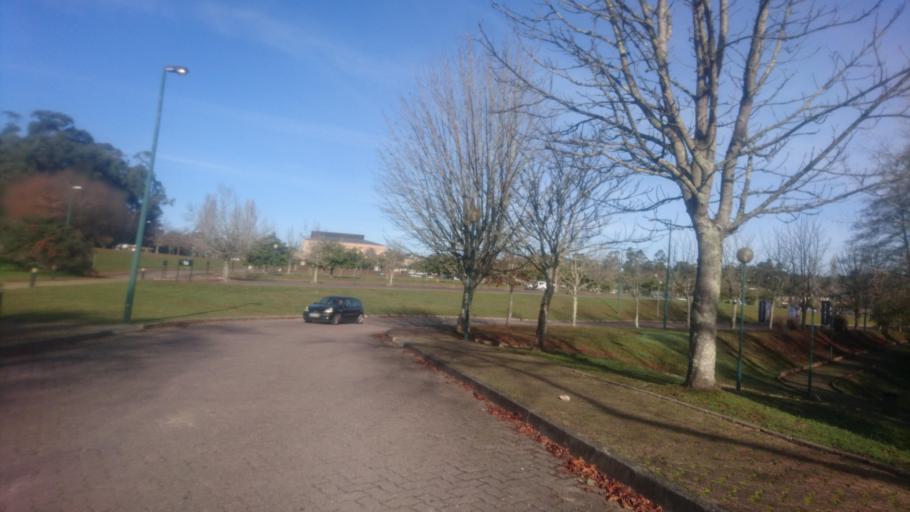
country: PT
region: Aveiro
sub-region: Santa Maria da Feira
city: Rio Meao
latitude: 40.9320
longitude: -8.5769
